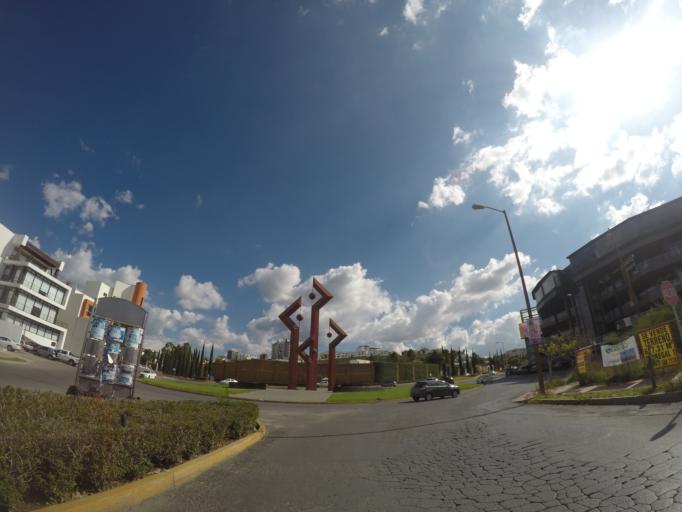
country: MX
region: San Luis Potosi
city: Escalerillas
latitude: 22.1294
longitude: -101.0341
